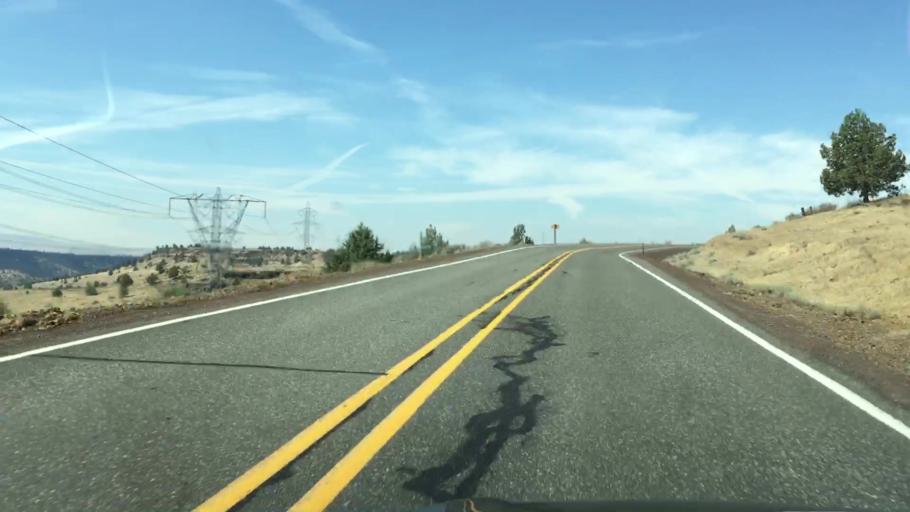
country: US
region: Oregon
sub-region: Wasco County
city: The Dalles
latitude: 45.1675
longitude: -121.1118
